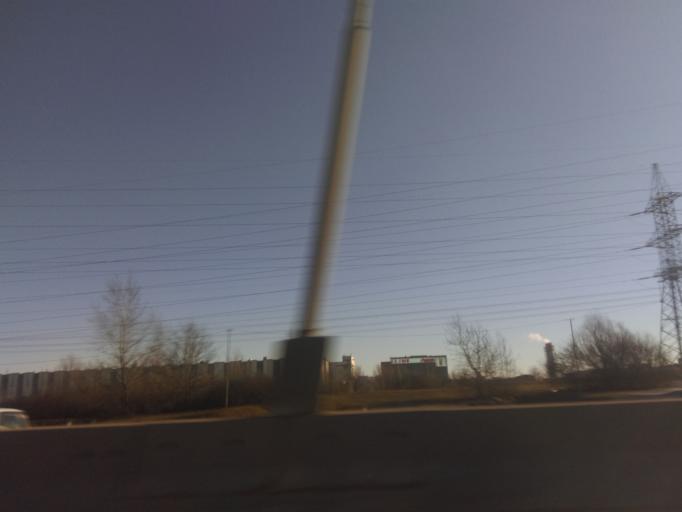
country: RU
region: Moscow
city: Mikhalkovo
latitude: 55.6735
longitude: 37.4235
